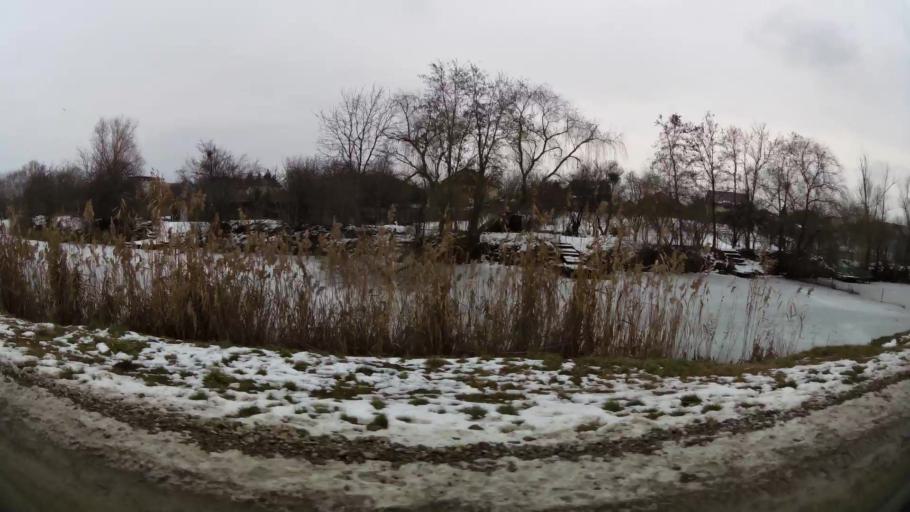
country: RO
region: Ilfov
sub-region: Comuna Tunari
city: Tunari
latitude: 44.5531
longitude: 26.1464
